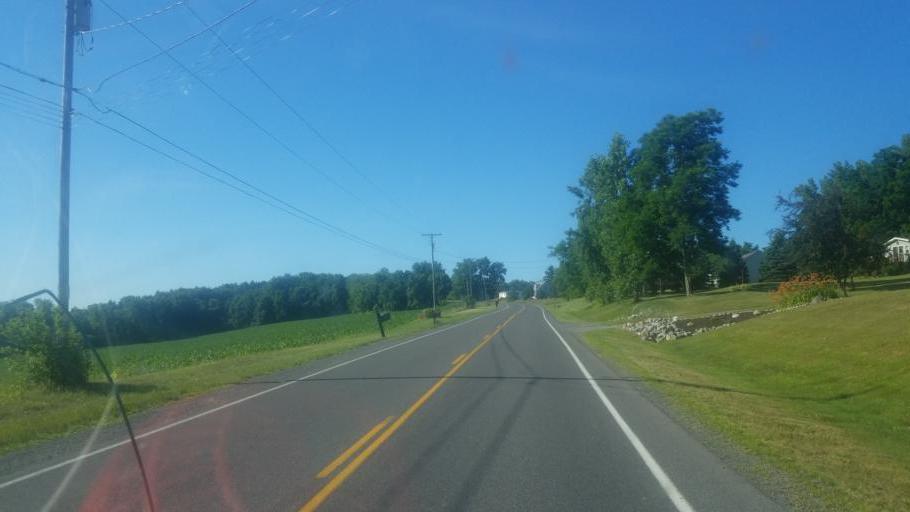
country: US
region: New York
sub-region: Ontario County
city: Phelps
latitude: 42.9288
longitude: -77.0678
